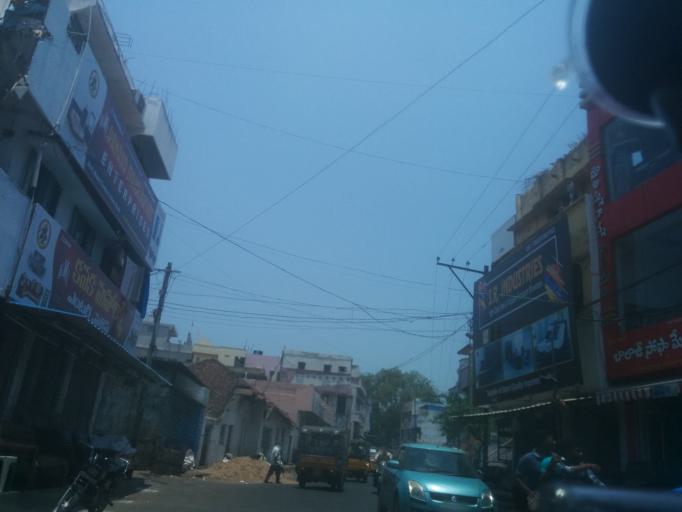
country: IN
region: Andhra Pradesh
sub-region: East Godavari
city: Rajahmundry
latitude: 16.9994
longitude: 81.7756
